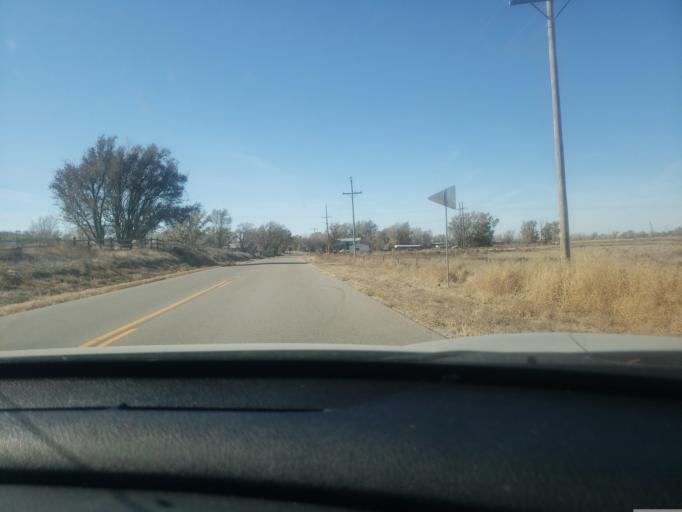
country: US
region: Kansas
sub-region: Finney County
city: Garden City
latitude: 37.9514
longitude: -100.8635
